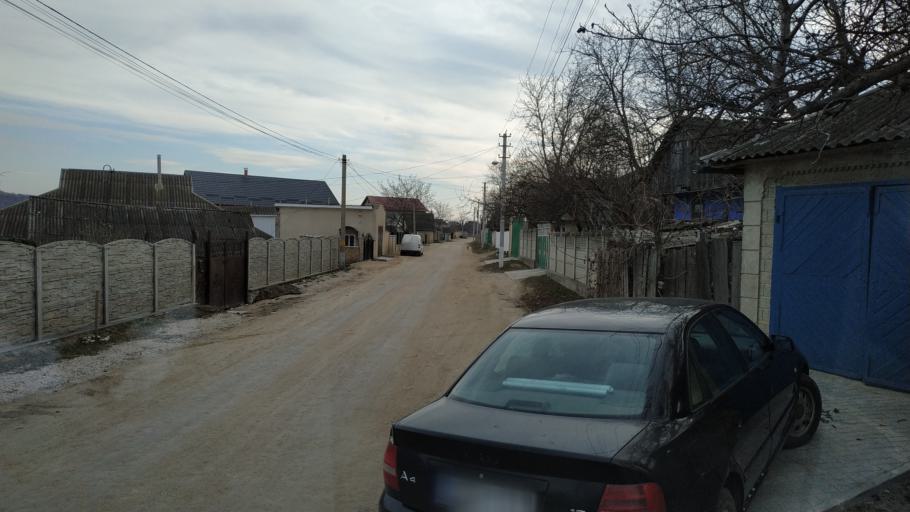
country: MD
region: Nisporeni
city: Nisporeni
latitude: 47.0827
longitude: 28.1751
